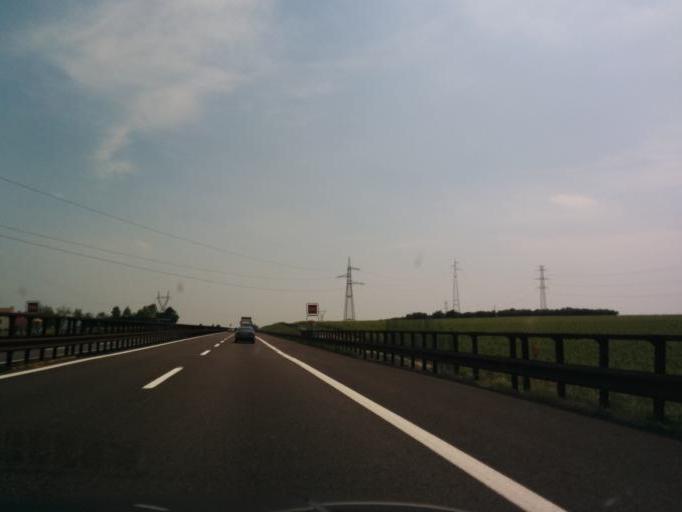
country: IT
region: Veneto
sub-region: Provincia di Verona
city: Cavajon Veronese
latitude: 45.5245
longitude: 10.7819
